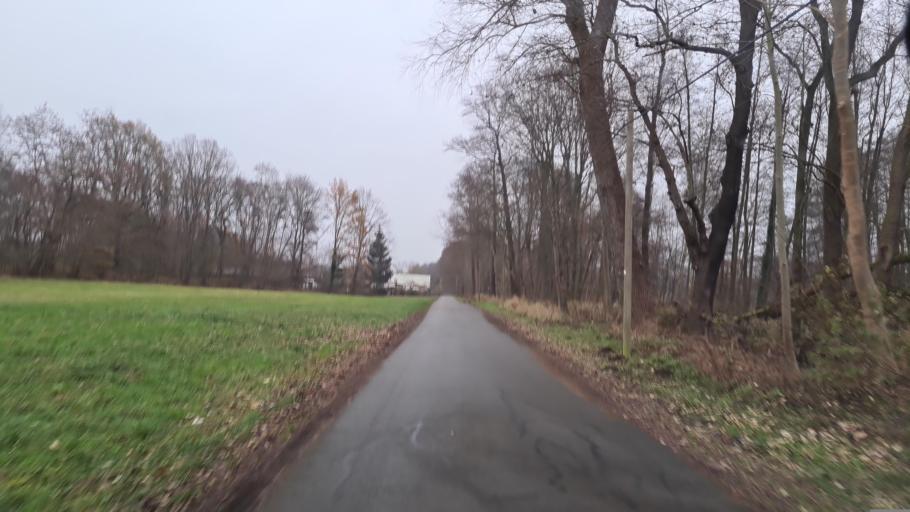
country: DE
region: Brandenburg
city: Kolkwitz
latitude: 51.7480
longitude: 14.2673
